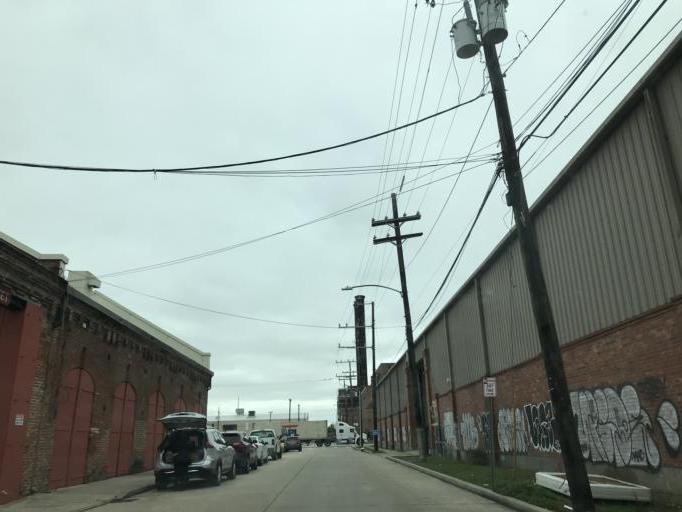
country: US
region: Louisiana
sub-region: Jefferson Parish
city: Gretna
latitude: 29.9314
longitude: -90.0681
